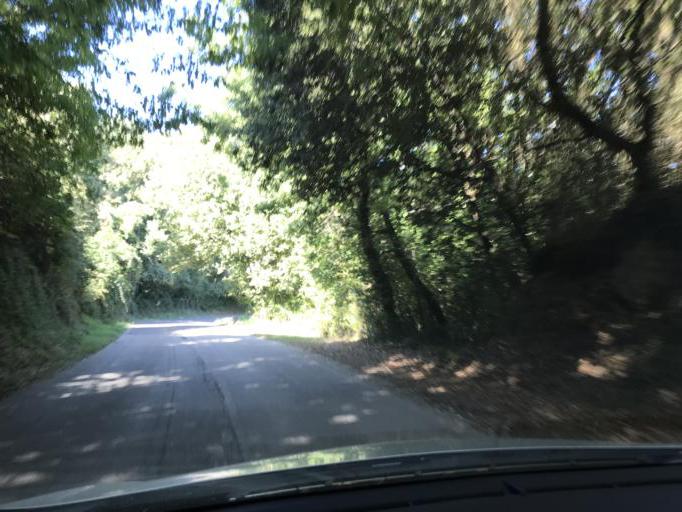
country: IT
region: Umbria
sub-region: Provincia di Terni
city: Avigliano Umbro
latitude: 42.6168
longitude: 12.4090
